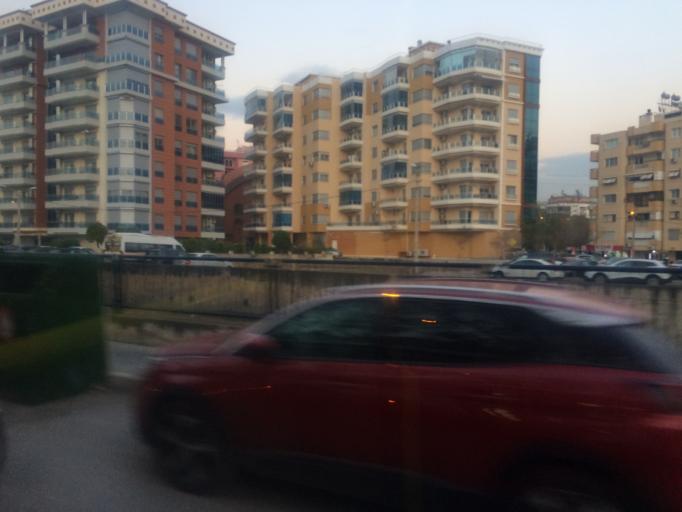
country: TR
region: Izmir
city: Karsiyaka
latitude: 38.4620
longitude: 27.0962
